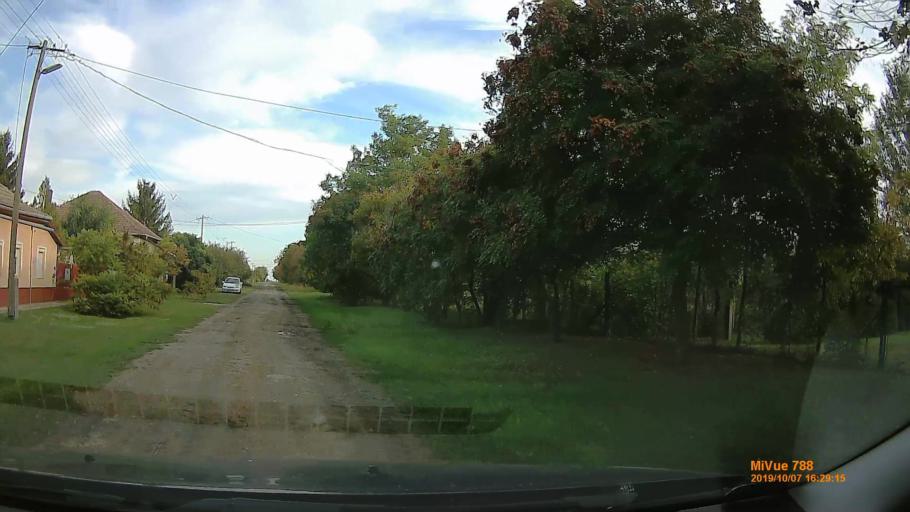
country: HU
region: Bekes
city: Szarvas
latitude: 46.8195
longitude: 20.6501
